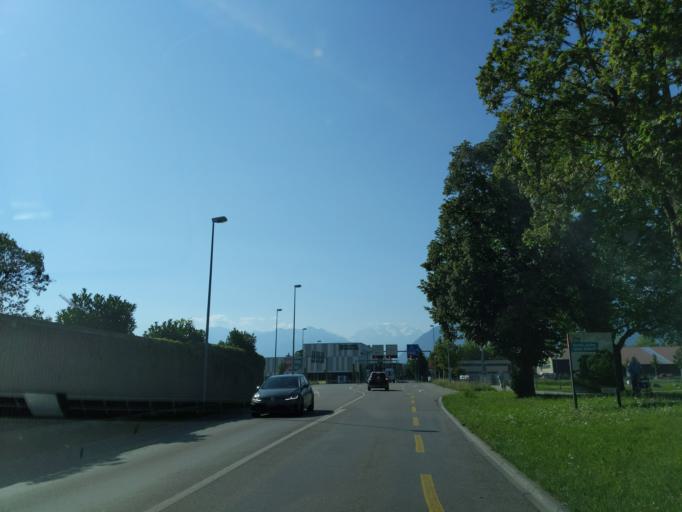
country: CH
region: Bern
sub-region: Thun District
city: Thun
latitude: 46.7463
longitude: 7.6122
